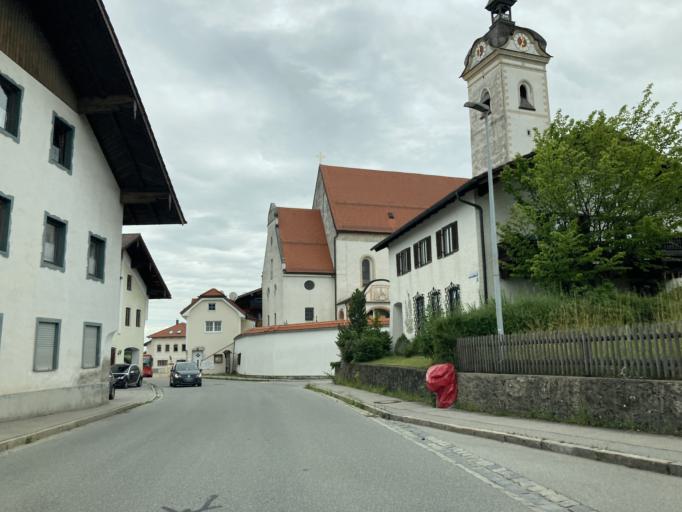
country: DE
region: Bavaria
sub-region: Upper Bavaria
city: Vogtareuth
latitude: 47.9474
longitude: 12.1814
